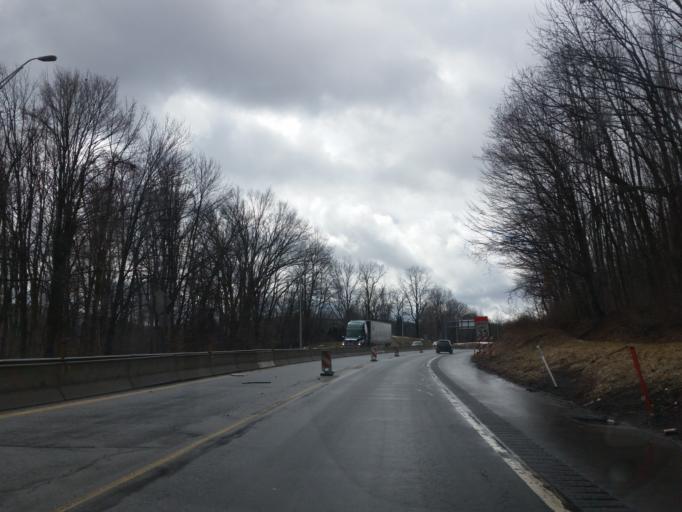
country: US
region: Pennsylvania
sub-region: Lackawanna County
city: Chinchilla
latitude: 41.4885
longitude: -75.6833
